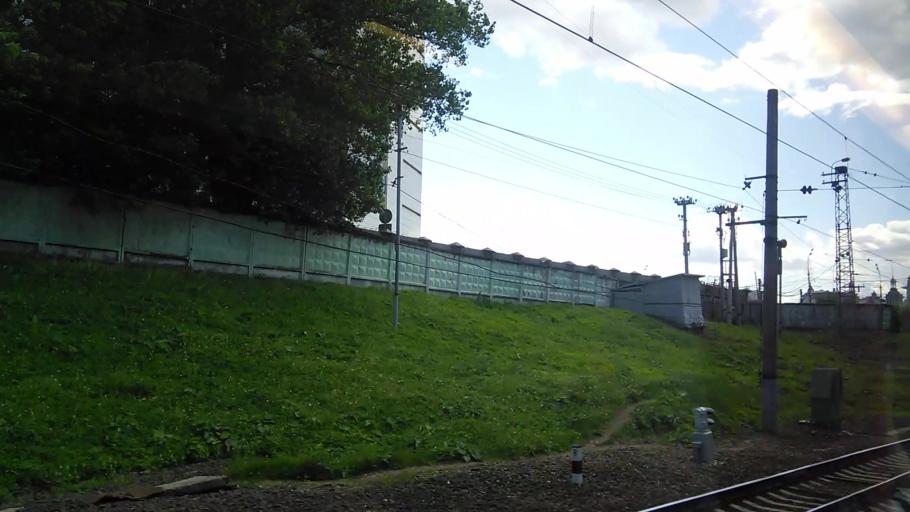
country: RU
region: Moskovskaya
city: Dorogomilovo
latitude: 55.7788
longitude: 37.5842
